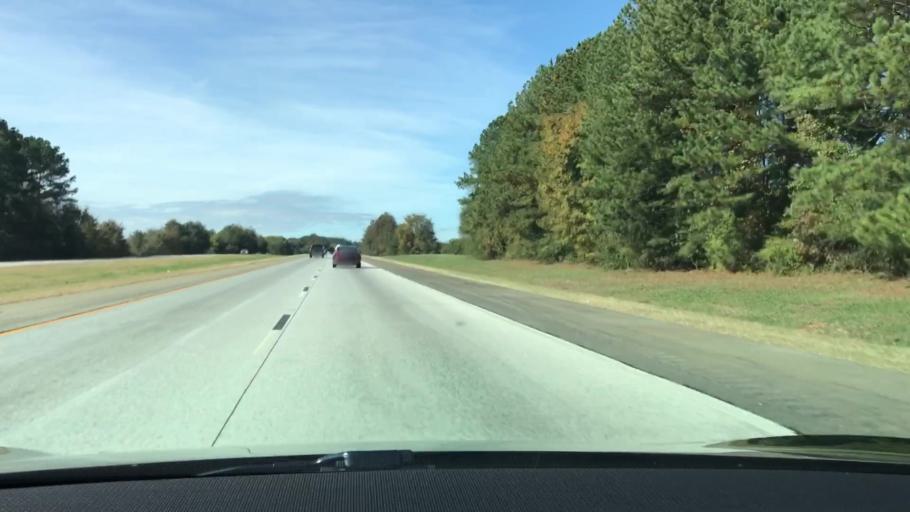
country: US
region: Georgia
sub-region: Morgan County
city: Madison
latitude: 33.5541
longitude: -83.3992
